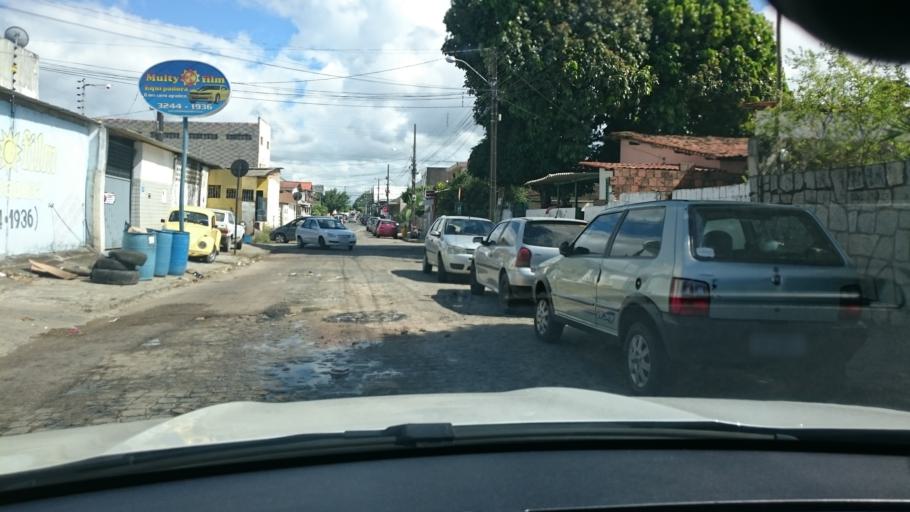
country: BR
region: Paraiba
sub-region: Joao Pessoa
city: Joao Pessoa
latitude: -7.1267
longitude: -34.8621
